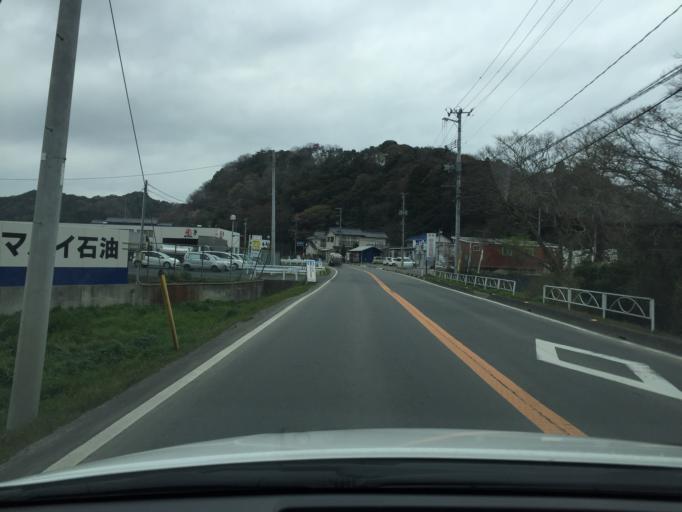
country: JP
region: Fukushima
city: Iwaki
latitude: 36.9906
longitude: 140.9671
